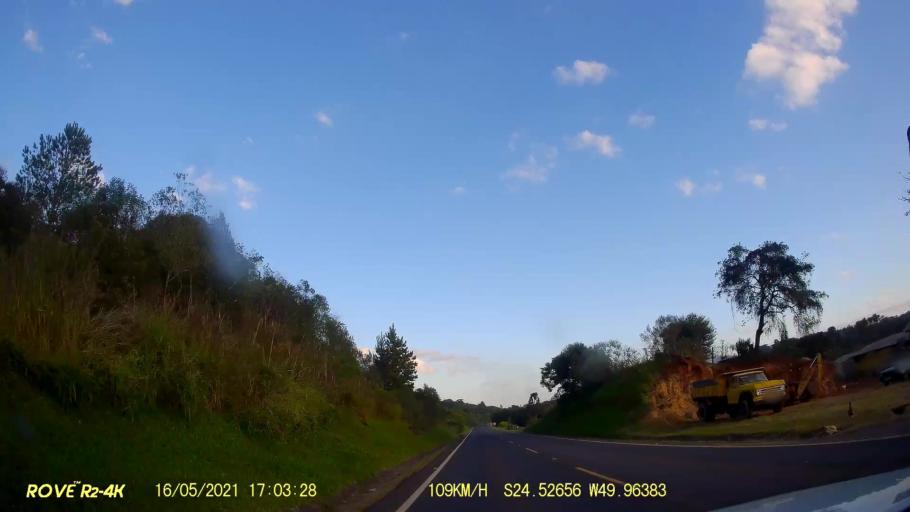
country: BR
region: Parana
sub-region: Pirai Do Sul
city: Pirai do Sul
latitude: -24.5263
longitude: -49.9639
